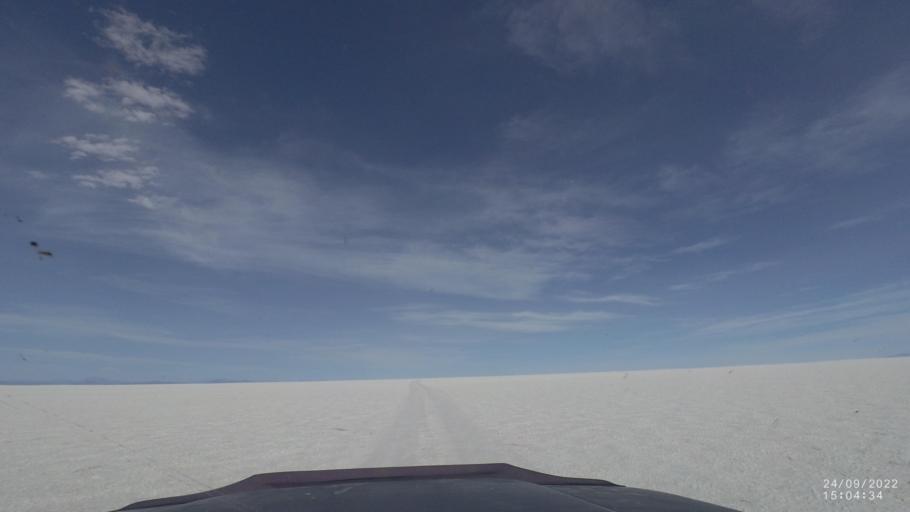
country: BO
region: Potosi
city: Colchani
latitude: -19.9006
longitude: -67.5234
